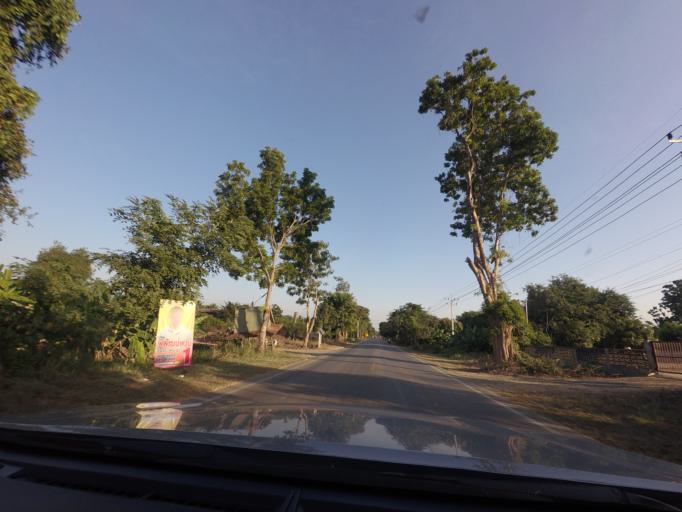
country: TH
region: Sukhothai
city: Sawankhalok
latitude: 17.3624
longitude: 99.8106
